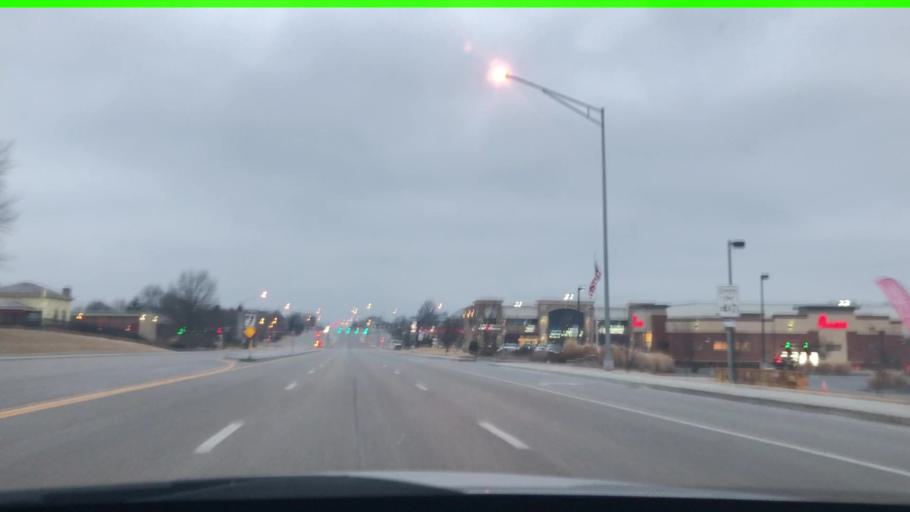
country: US
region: Missouri
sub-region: Boone County
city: Columbia
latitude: 38.9604
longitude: -92.3714
